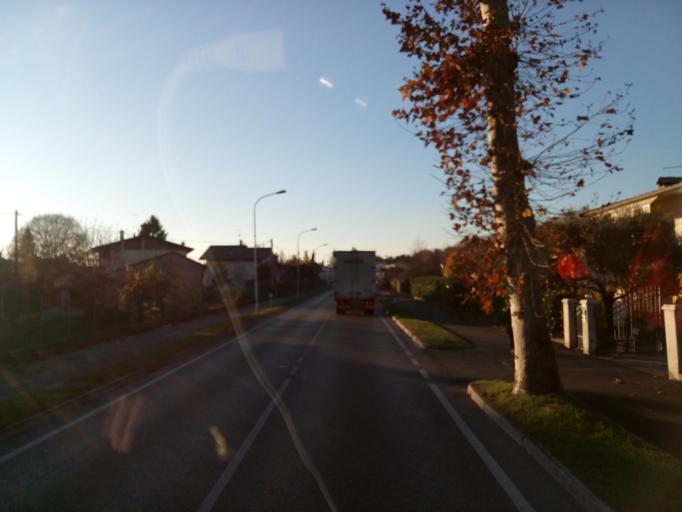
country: IT
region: Veneto
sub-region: Provincia di Treviso
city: San Zenone degli Ezzelini
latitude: 45.7797
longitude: 11.8522
